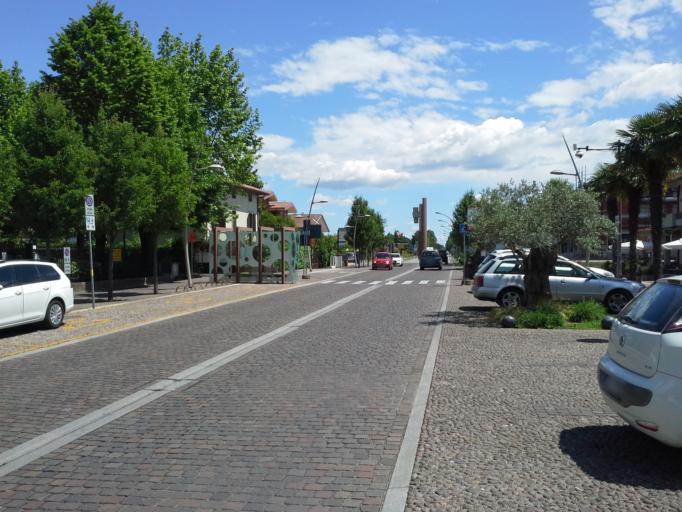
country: IT
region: Lombardy
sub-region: Provincia di Brescia
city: San Martino della Battaglia
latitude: 45.4615
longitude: 10.6227
